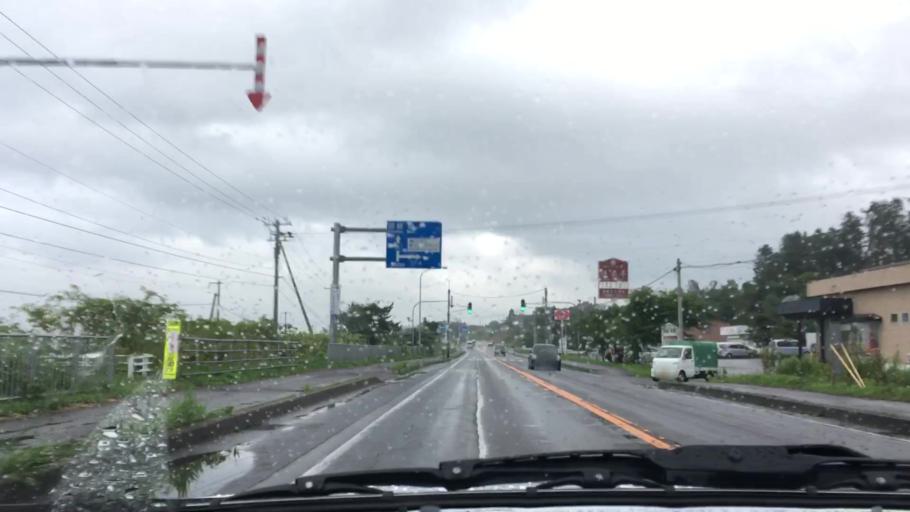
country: JP
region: Hokkaido
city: Nanae
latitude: 42.2361
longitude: 140.3094
